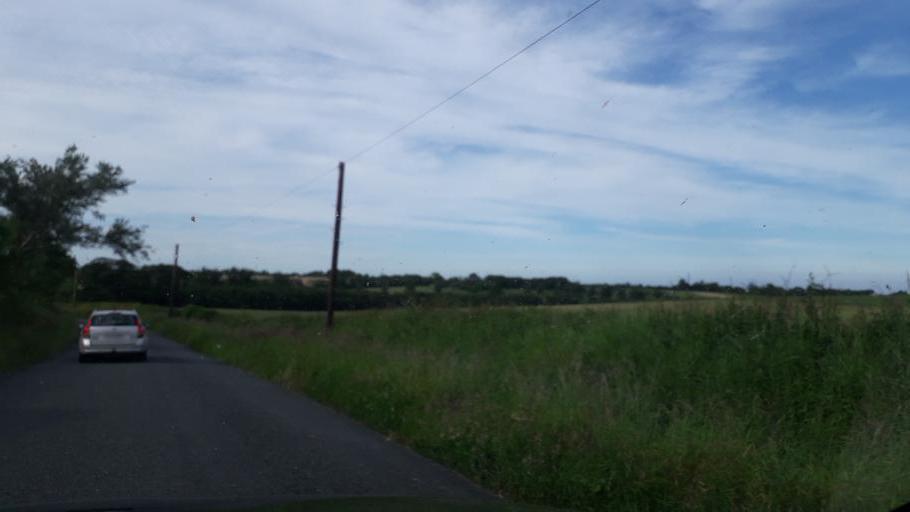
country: IE
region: Leinster
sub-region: Loch Garman
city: Courtown
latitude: 52.5397
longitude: -6.2536
